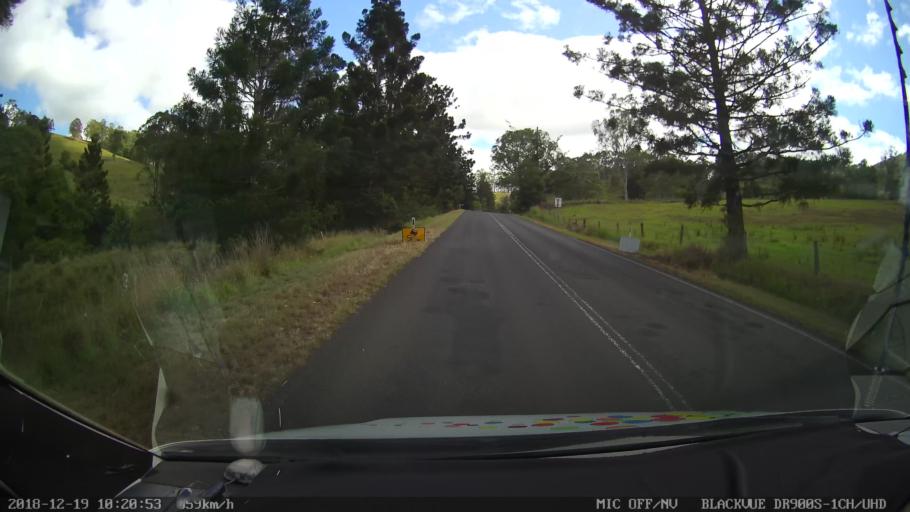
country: AU
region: New South Wales
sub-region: Kyogle
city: Kyogle
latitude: -28.6022
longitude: 153.0570
